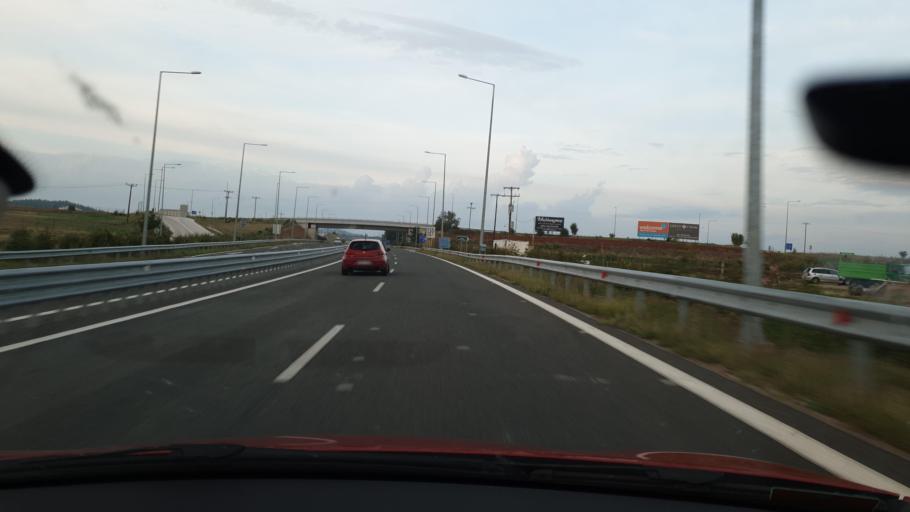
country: GR
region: Central Macedonia
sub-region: Nomos Kilkis
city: Kristoni
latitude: 40.9581
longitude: 22.8511
